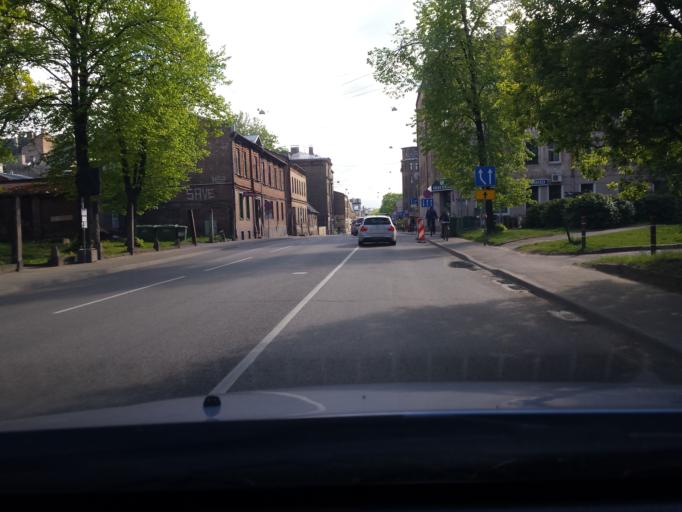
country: LV
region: Riga
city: Riga
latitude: 56.9512
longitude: 24.1495
